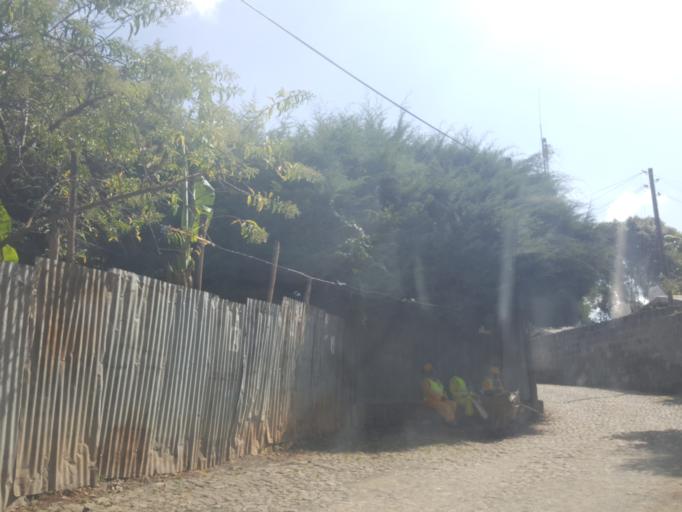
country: ET
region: Adis Abeba
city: Addis Ababa
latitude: 9.0530
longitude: 38.7327
